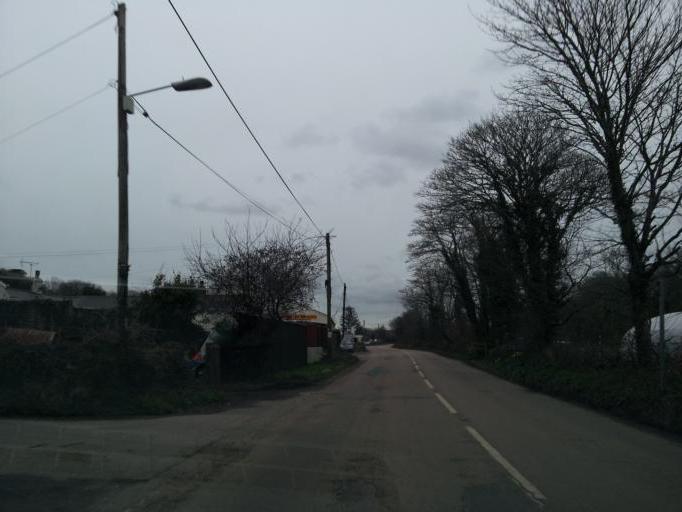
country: GB
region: England
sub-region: Cornwall
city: Redruth
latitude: 50.2590
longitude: -5.2589
